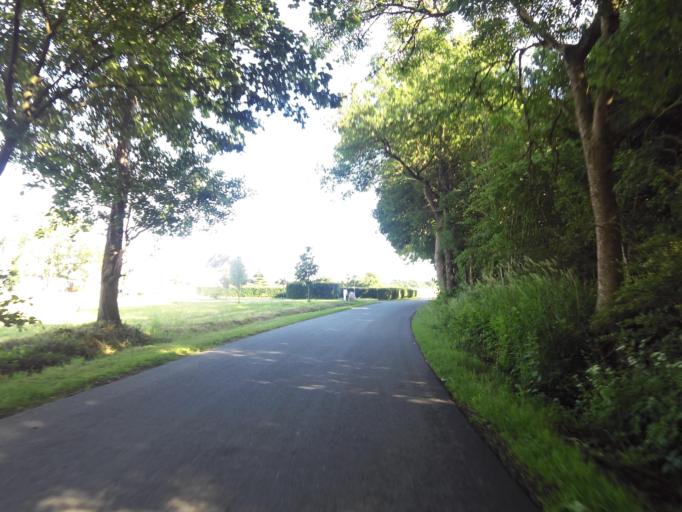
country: DK
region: South Denmark
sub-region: Vejen Kommune
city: Rodding
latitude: 55.3611
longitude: 9.0691
